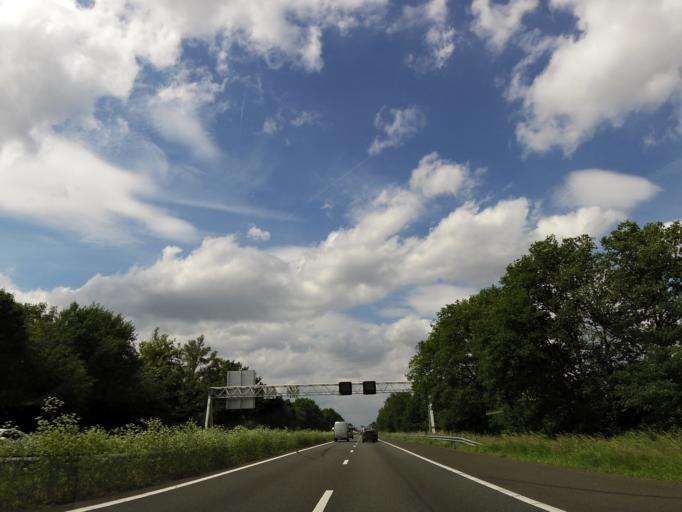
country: NL
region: Limburg
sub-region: Gemeente Leudal
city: Kelpen-Oler
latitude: 51.1901
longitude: 5.8388
